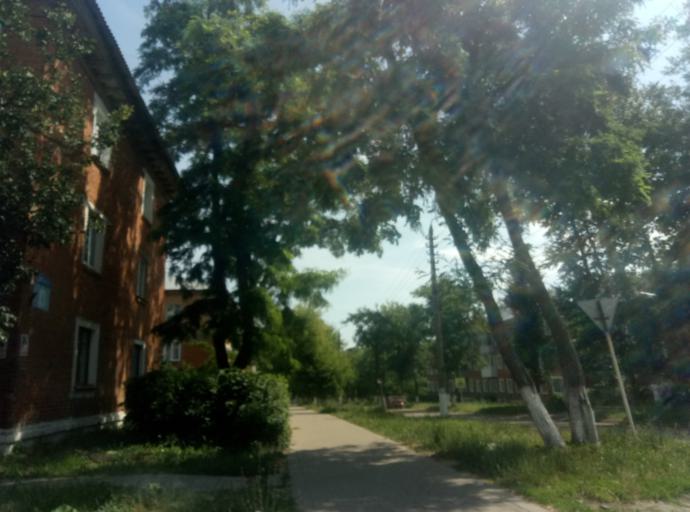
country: RU
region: Tula
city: Kireyevsk
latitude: 53.9285
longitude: 37.9338
